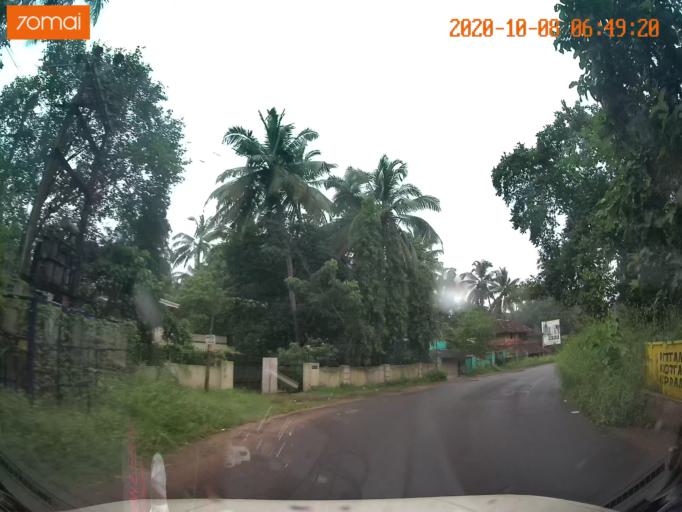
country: IN
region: Kerala
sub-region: Thrissur District
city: Kunnamkulam
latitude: 10.6826
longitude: 76.1029
